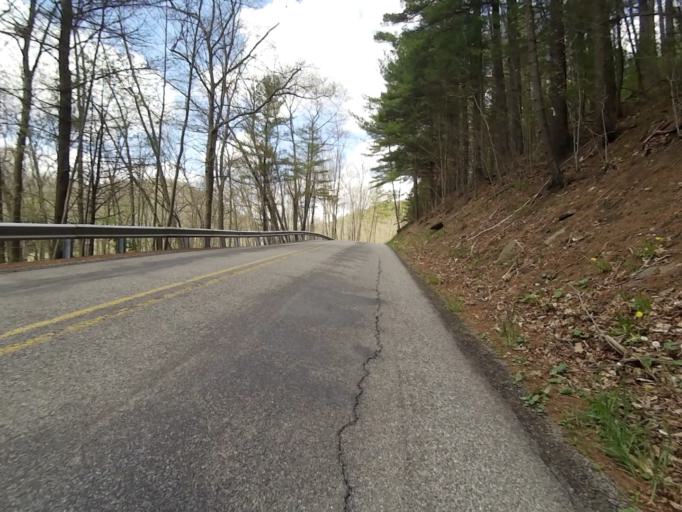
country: US
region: Pennsylvania
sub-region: Centre County
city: Milesburg
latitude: 40.9349
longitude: -77.8769
